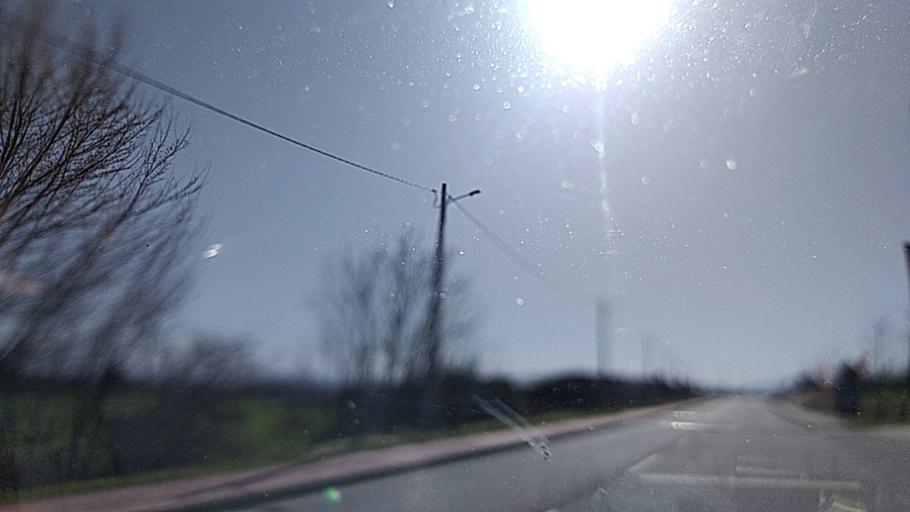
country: PT
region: Guarda
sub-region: Celorico da Beira
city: Celorico da Beira
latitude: 40.6521
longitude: -7.3835
